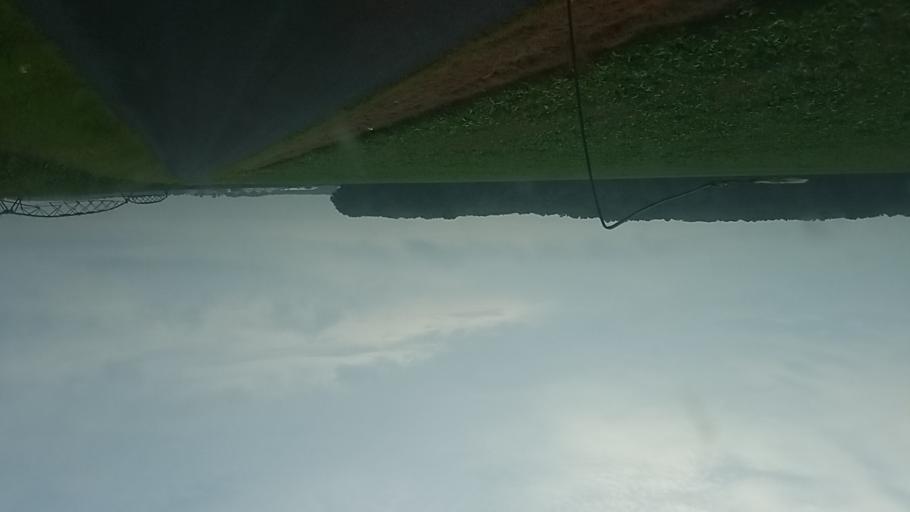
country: US
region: Delaware
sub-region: Sussex County
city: Selbyville
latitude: 38.4473
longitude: -75.2765
